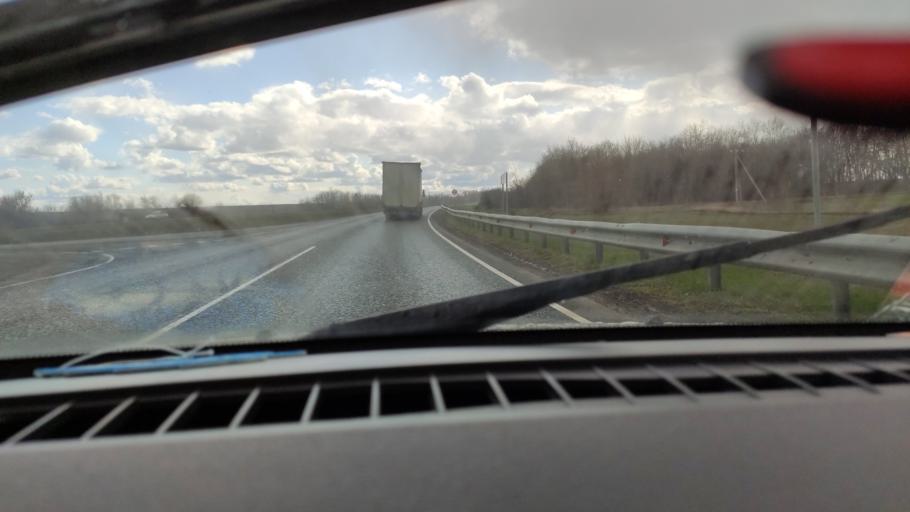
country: RU
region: Saratov
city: Balakovo
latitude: 52.1071
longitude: 47.7445
